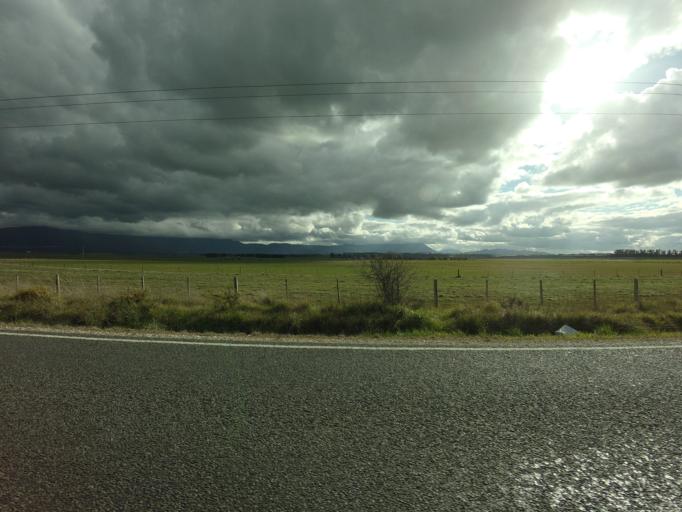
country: AU
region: Tasmania
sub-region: Northern Midlands
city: Longford
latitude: -41.7463
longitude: 147.0823
